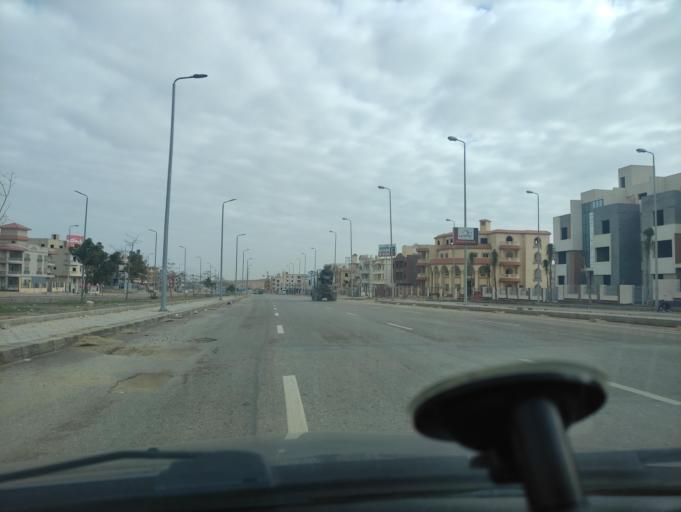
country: EG
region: Muhafazat al Qalyubiyah
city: Al Khankah
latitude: 30.0468
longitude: 31.5277
